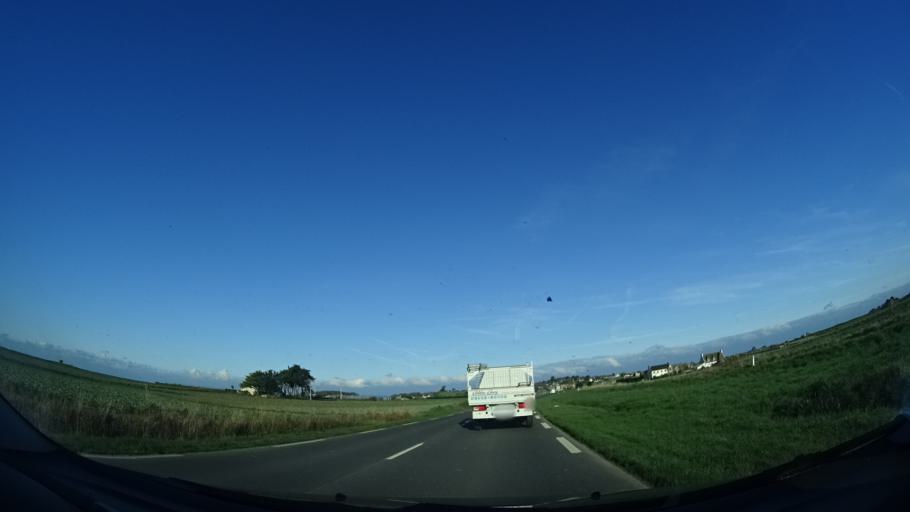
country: FR
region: Brittany
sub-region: Departement du Finistere
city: Saint-Pol-de-Leon
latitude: 48.6930
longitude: -3.9987
